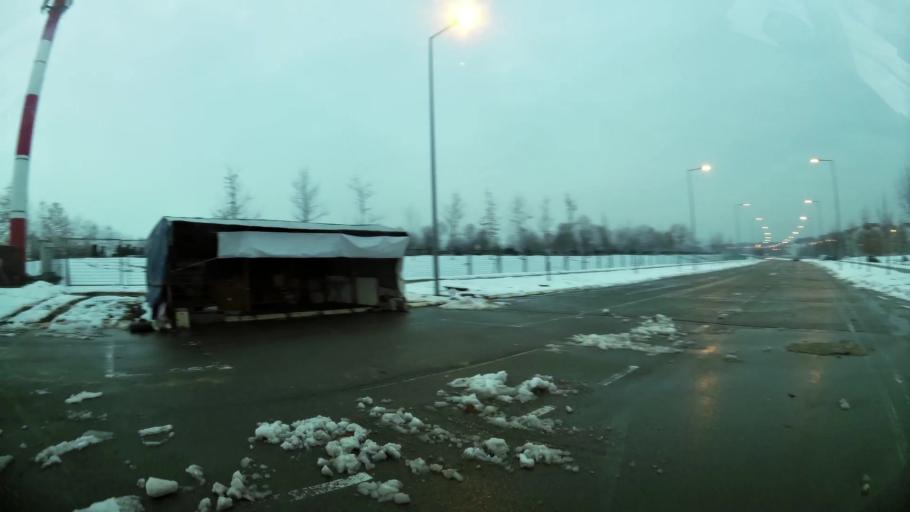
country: RS
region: Central Serbia
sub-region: Belgrade
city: Zemun
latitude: 44.8098
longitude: 20.3618
